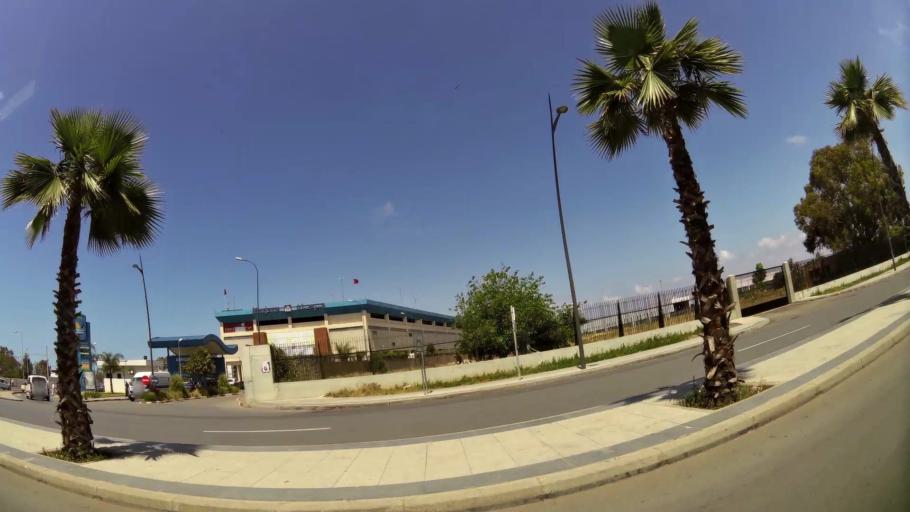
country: MA
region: Rabat-Sale-Zemmour-Zaer
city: Sale
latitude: 34.0507
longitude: -6.7970
